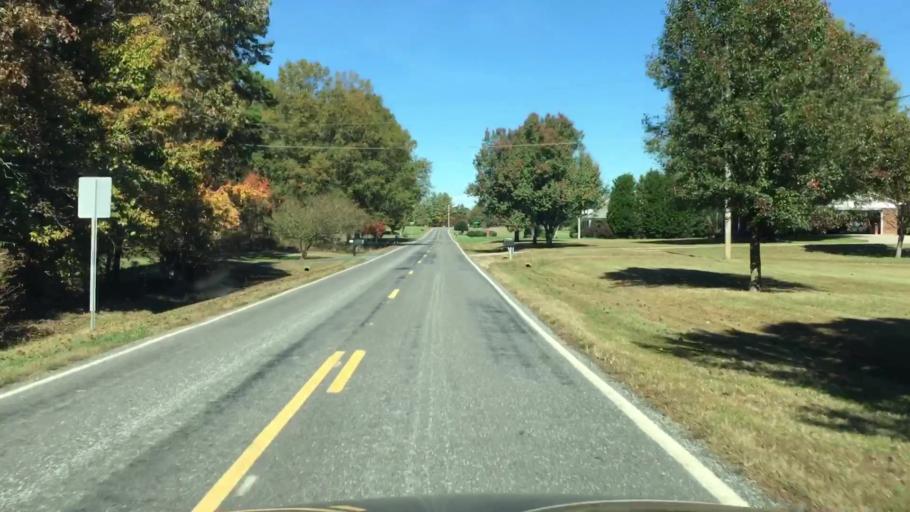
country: US
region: North Carolina
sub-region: Iredell County
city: Mooresville
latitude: 35.5815
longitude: -80.7617
